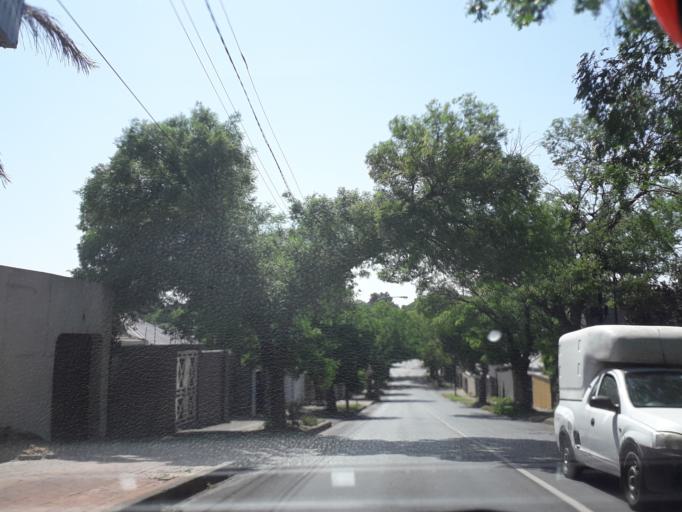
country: ZA
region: Gauteng
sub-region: City of Johannesburg Metropolitan Municipality
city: Johannesburg
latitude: -26.1560
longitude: 28.0689
